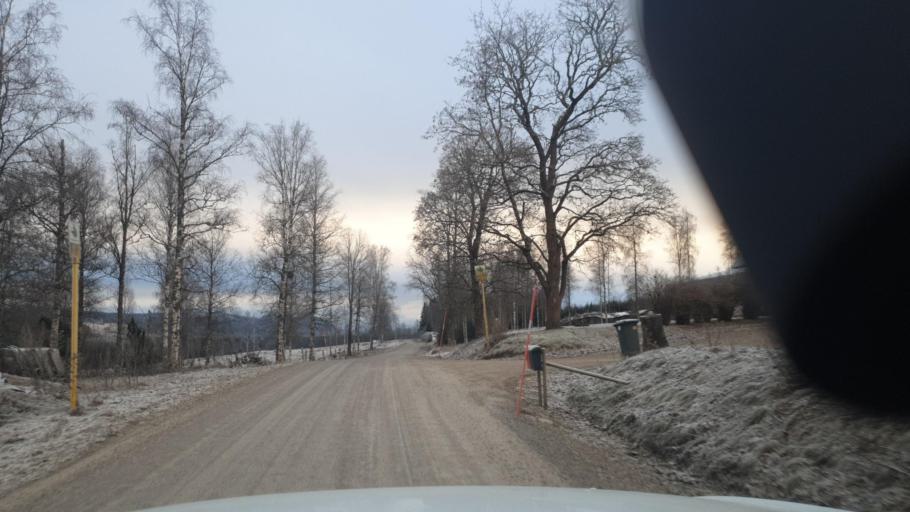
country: SE
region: Vaermland
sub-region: Torsby Kommun
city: Torsby
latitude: 59.9546
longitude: 12.8928
